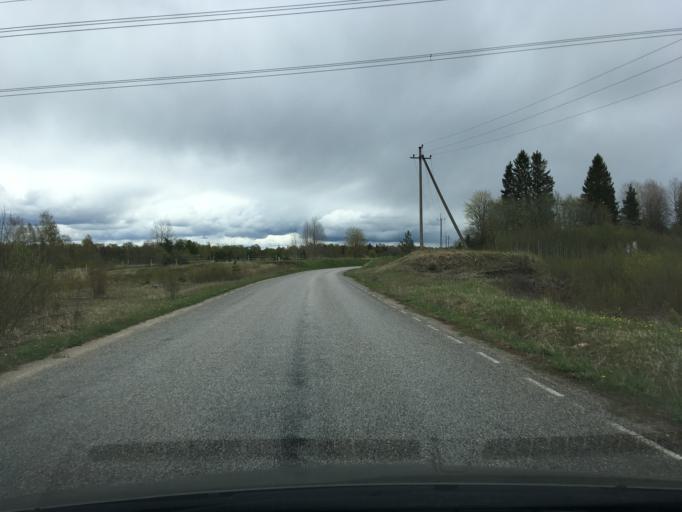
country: EE
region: Harju
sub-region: Rae vald
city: Vaida
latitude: 59.3469
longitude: 25.0053
